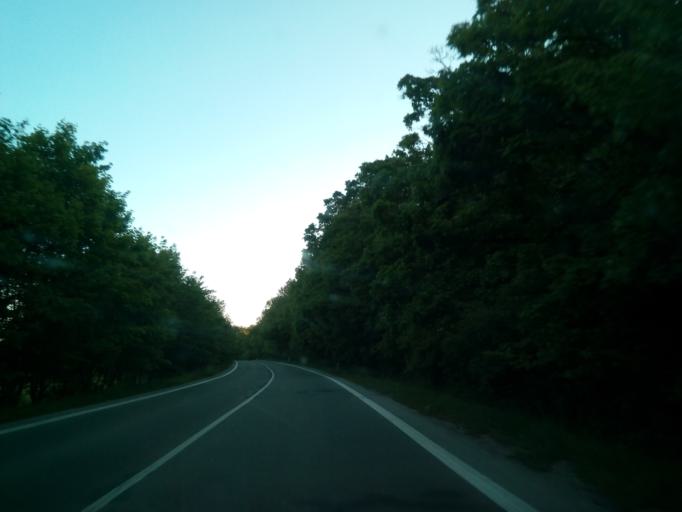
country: CZ
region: South Moravian
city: Bilovice nad Svitavou
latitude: 49.2227
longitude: 16.6846
